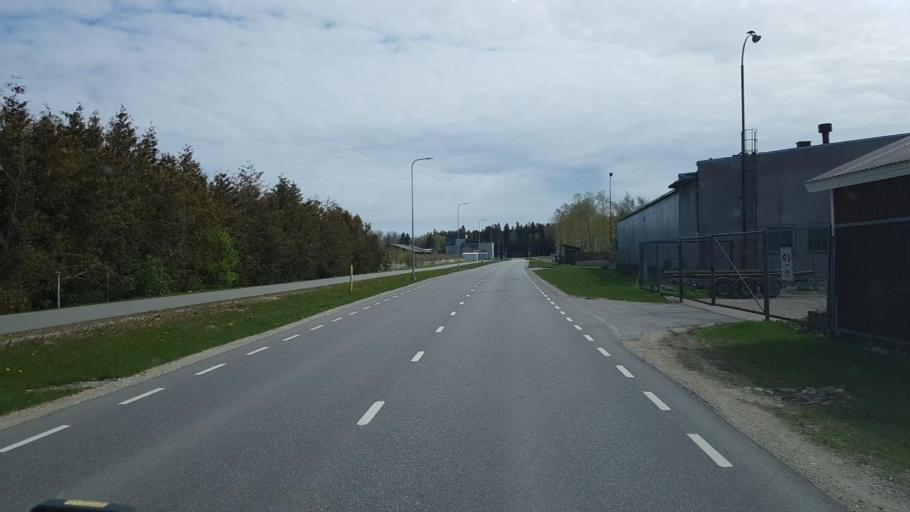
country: EE
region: Harju
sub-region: Viimsi vald
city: Rummu
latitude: 59.5395
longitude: 24.8001
